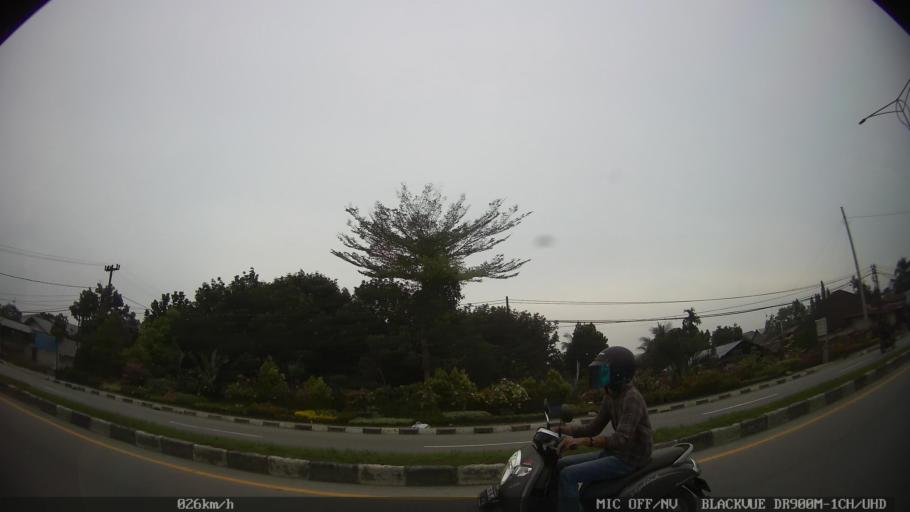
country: ID
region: North Sumatra
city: Deli Tua
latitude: 3.5326
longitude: 98.7313
